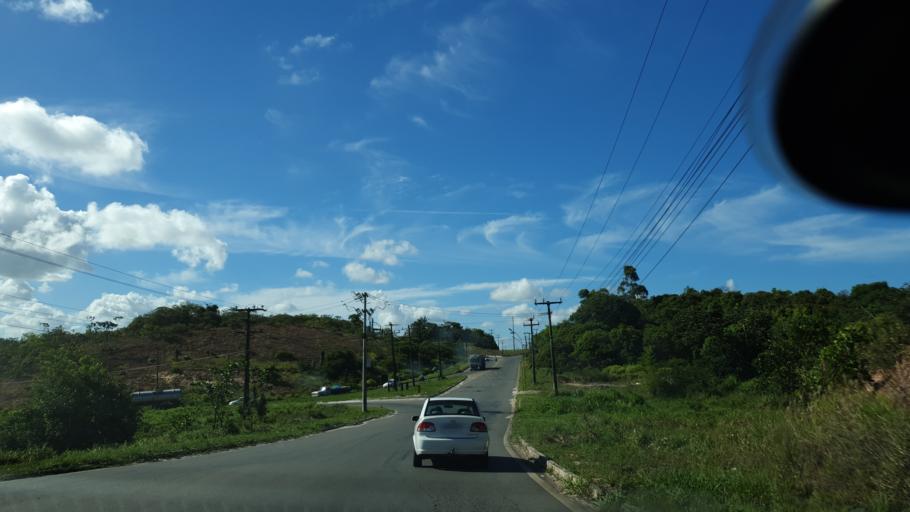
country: BR
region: Bahia
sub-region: Camacari
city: Camacari
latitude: -12.6832
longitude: -38.2803
